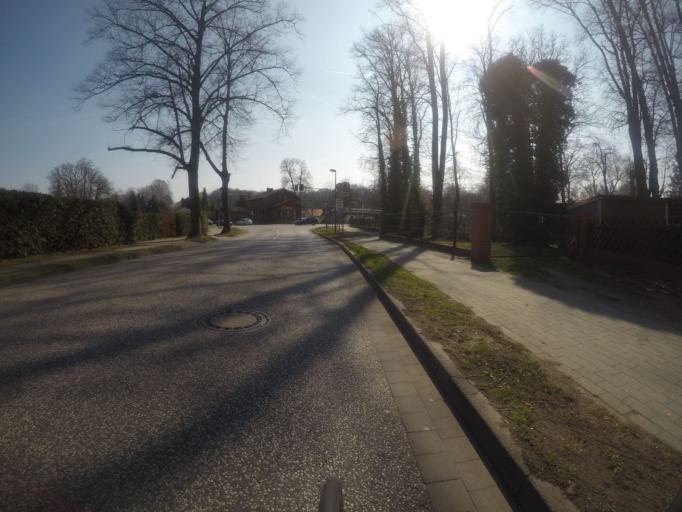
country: DE
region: Brandenburg
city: Konigs Wusterhausen
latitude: 52.2979
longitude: 13.6503
